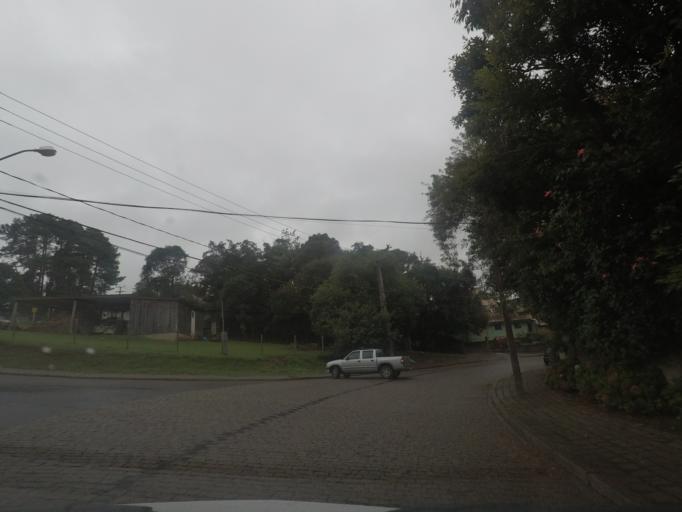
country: BR
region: Parana
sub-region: Quatro Barras
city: Quatro Barras
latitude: -25.3703
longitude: -49.0760
